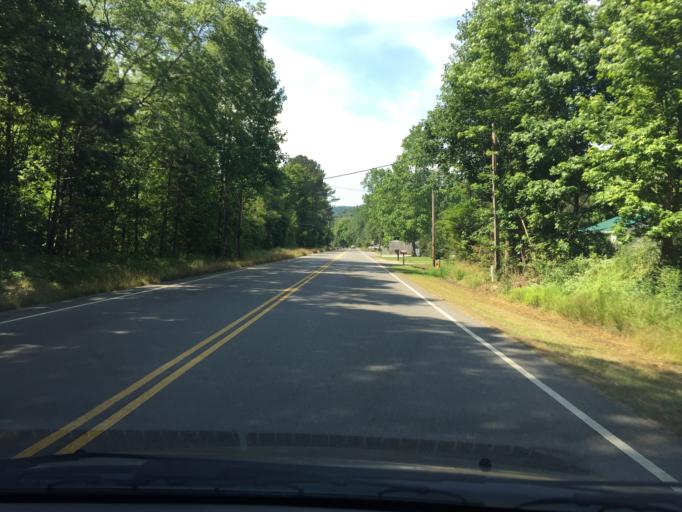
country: US
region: Tennessee
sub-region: Hamilton County
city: Collegedale
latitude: 35.1017
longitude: -85.0062
